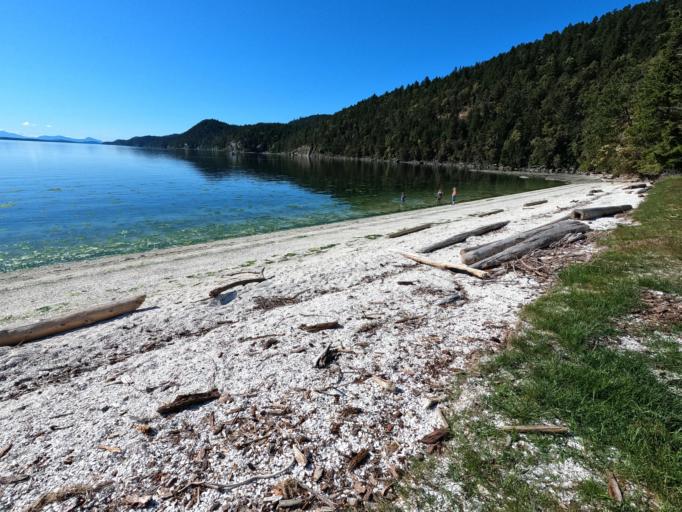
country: CA
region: British Columbia
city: North Saanich
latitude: 48.8984
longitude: -123.4082
